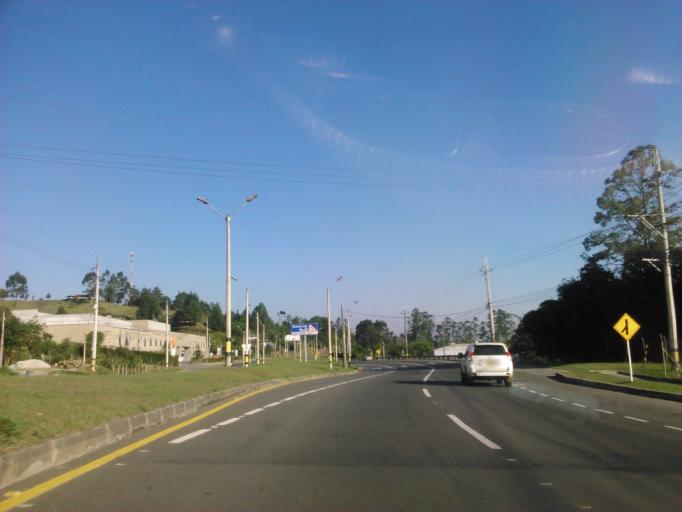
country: CO
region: Antioquia
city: San Vicente
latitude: 6.2238
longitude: -75.3917
